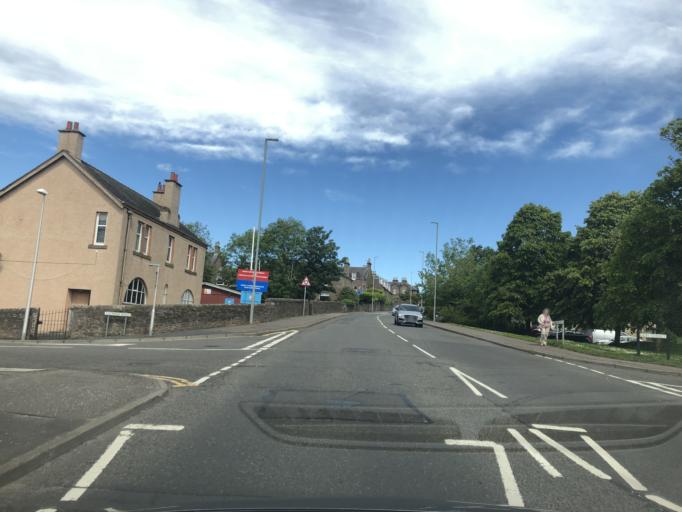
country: GB
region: Scotland
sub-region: Angus
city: Forfar
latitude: 56.6486
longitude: -2.8891
